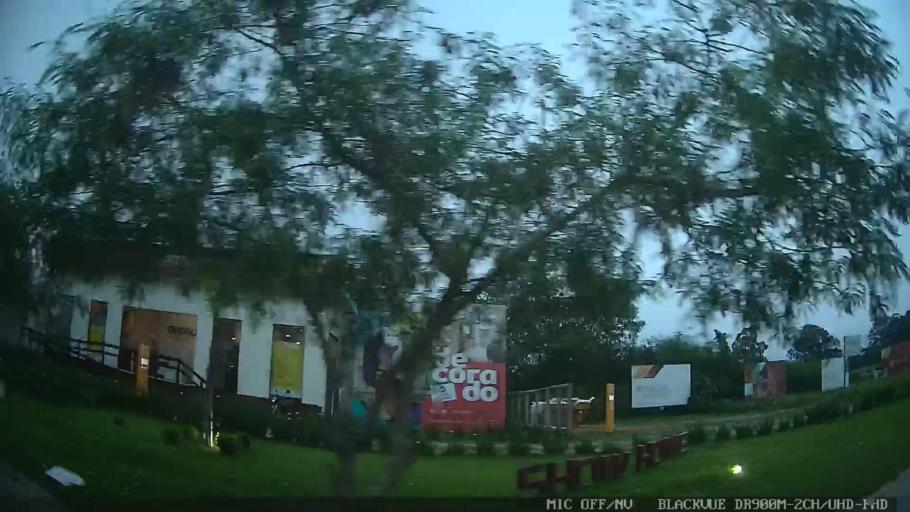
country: BR
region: Sao Paulo
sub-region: Mogi das Cruzes
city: Mogi das Cruzes
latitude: -23.5087
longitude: -46.1909
